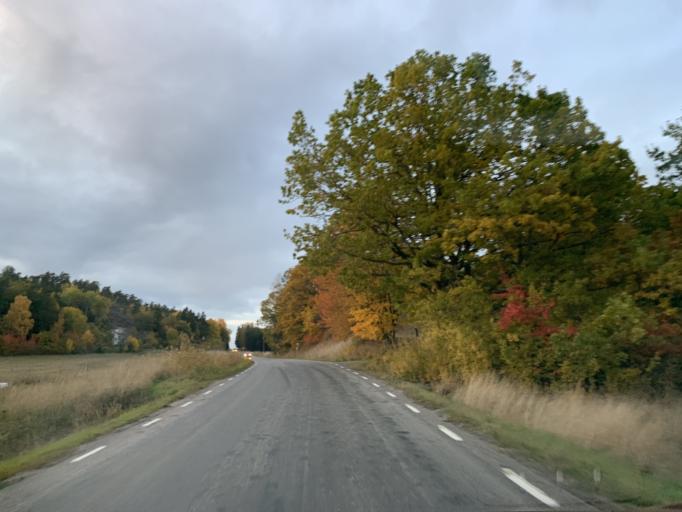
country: SE
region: Stockholm
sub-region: Nynashamns Kommun
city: Osmo
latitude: 58.9316
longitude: 17.7669
